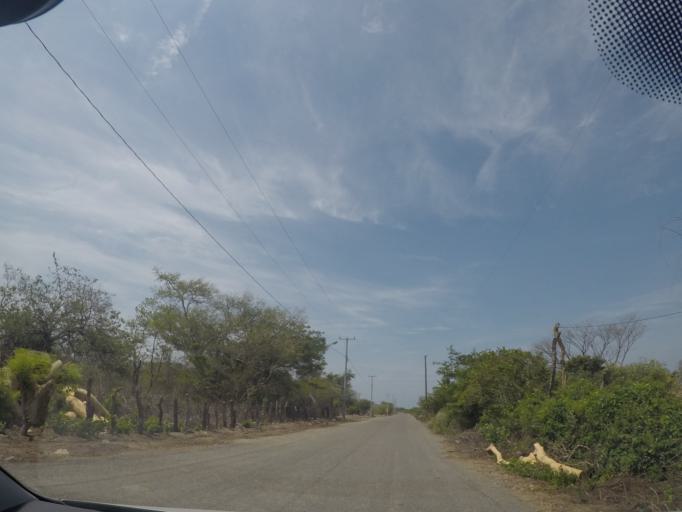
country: MX
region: Oaxaca
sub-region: Salina Cruz
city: Salina Cruz
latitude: 16.1991
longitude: -95.1200
